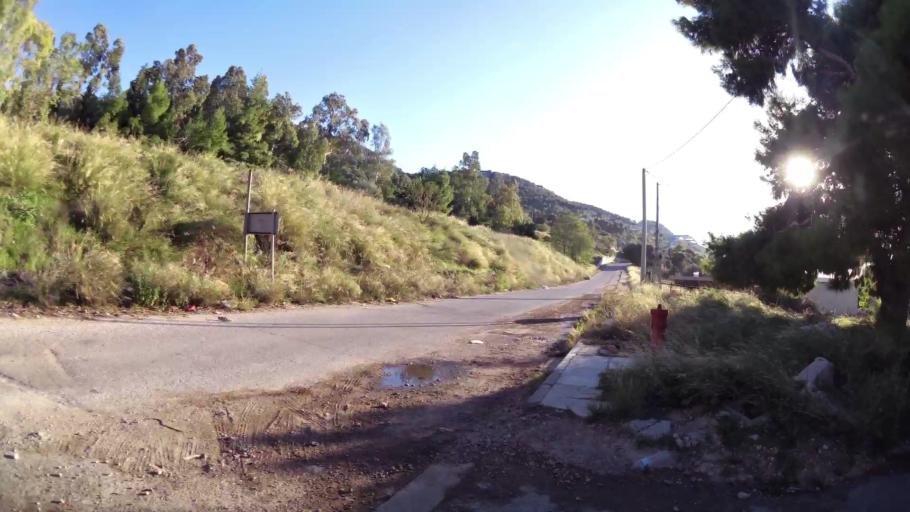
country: GR
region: Attica
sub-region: Nomarchia Athinas
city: Chaidari
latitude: 38.0344
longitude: 23.6355
